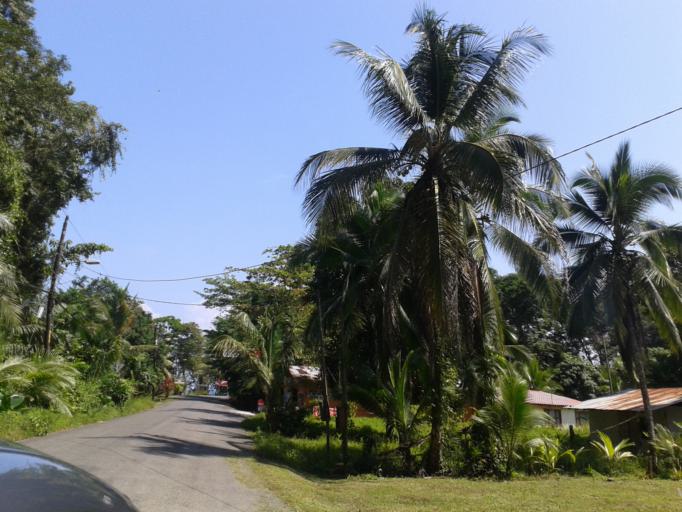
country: CR
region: Limon
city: Sixaola
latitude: 9.6302
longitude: -82.6614
